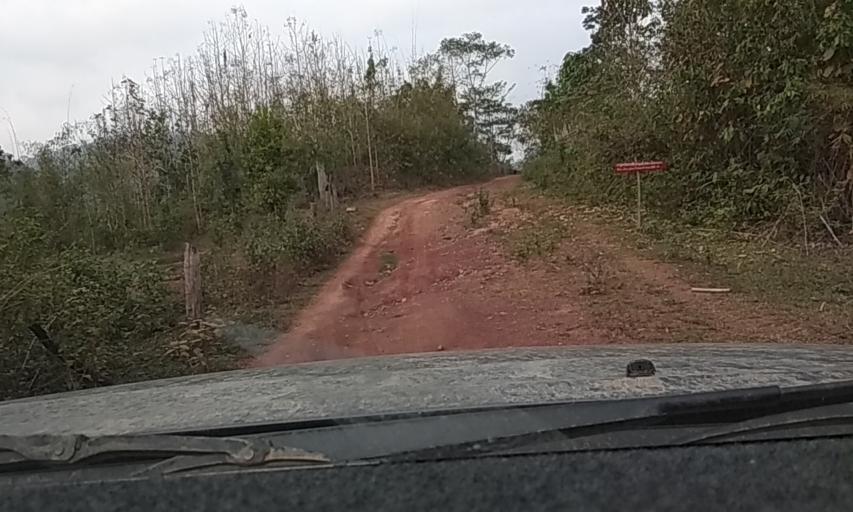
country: TH
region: Nan
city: Mae Charim
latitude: 18.4567
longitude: 101.1954
